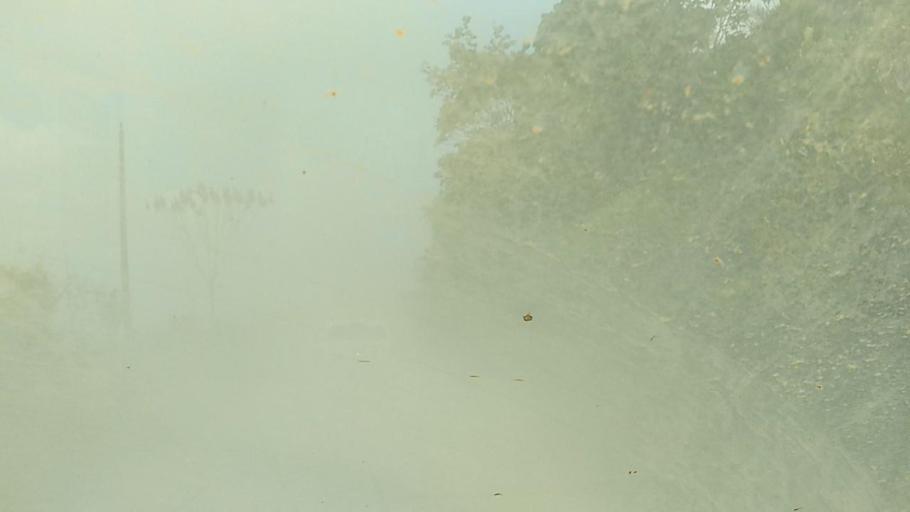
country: BR
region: Rondonia
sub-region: Porto Velho
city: Porto Velho
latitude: -8.7274
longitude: -63.3098
